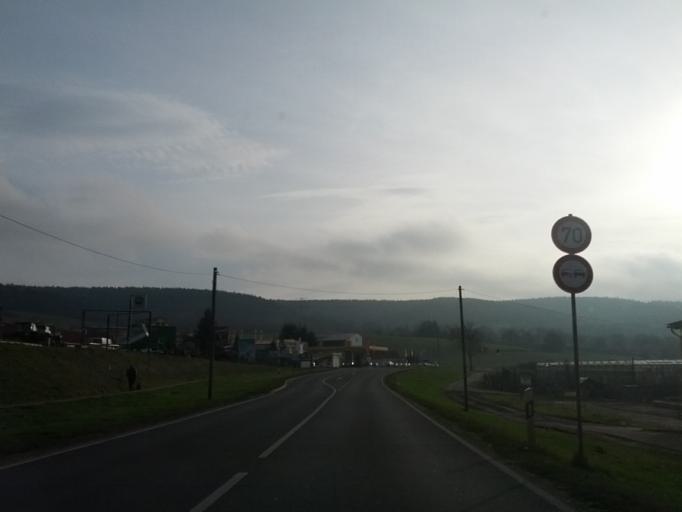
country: DE
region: Thuringia
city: Wasungen
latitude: 50.6561
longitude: 10.3752
